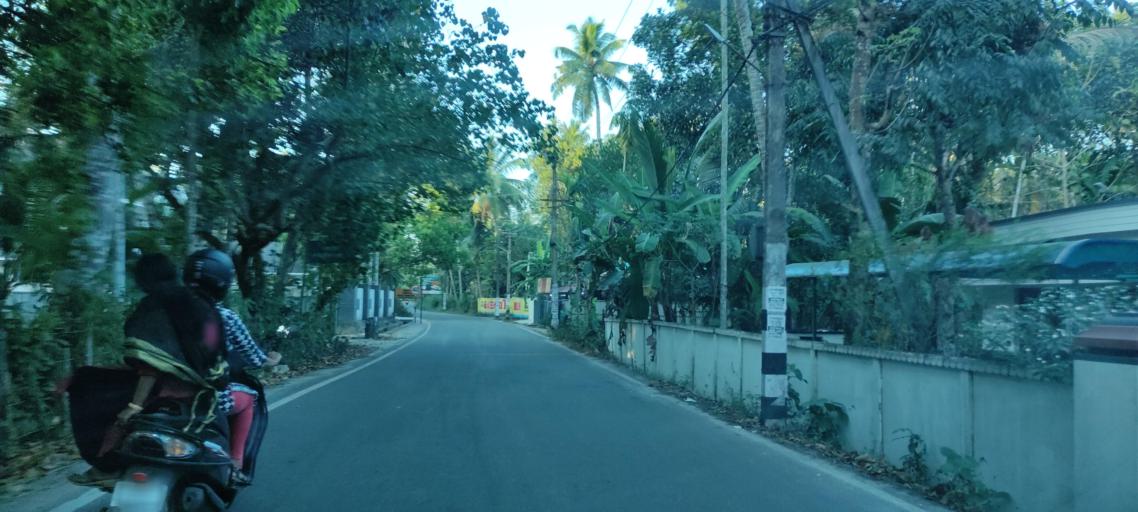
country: IN
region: Kerala
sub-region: Alappuzha
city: Kayankulam
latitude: 9.1986
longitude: 76.4646
